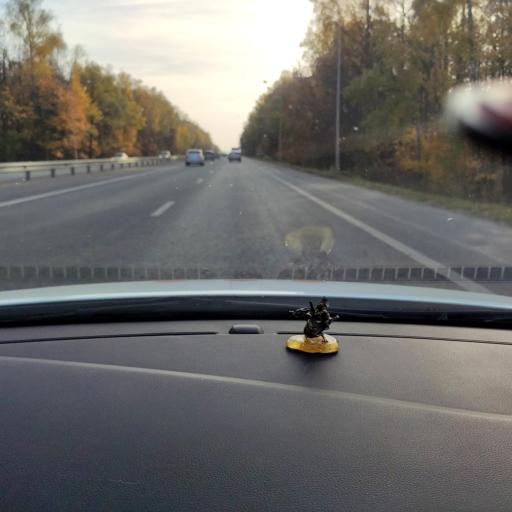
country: RU
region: Tatarstan
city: Osinovo
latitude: 55.8455
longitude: 48.8522
